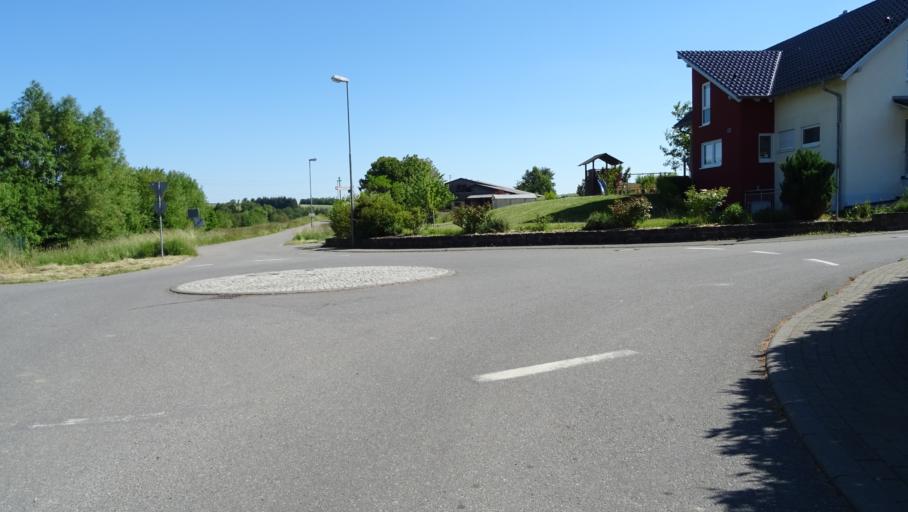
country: DE
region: Baden-Wuerttemberg
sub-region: Karlsruhe Region
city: Seckach
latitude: 49.4405
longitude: 9.2904
